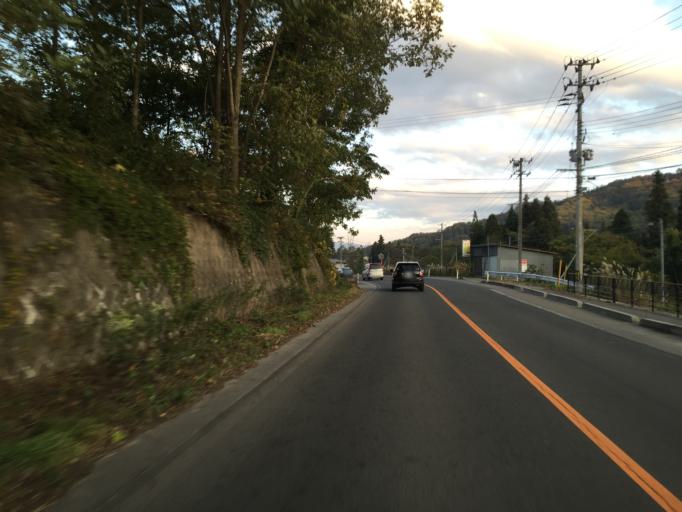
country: JP
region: Yamagata
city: Yonezawa
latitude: 37.9142
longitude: 140.0643
